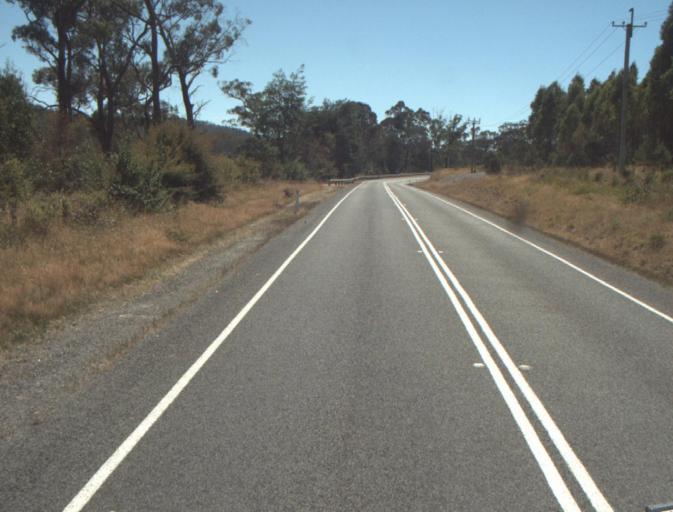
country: AU
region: Tasmania
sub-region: Launceston
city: Newstead
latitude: -41.3753
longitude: 147.3129
